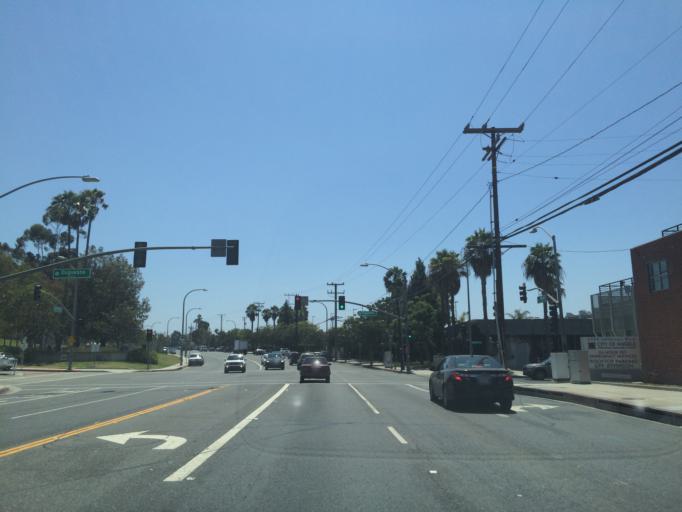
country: US
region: California
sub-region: Los Angeles County
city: Culver City
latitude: 34.0172
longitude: -118.3878
